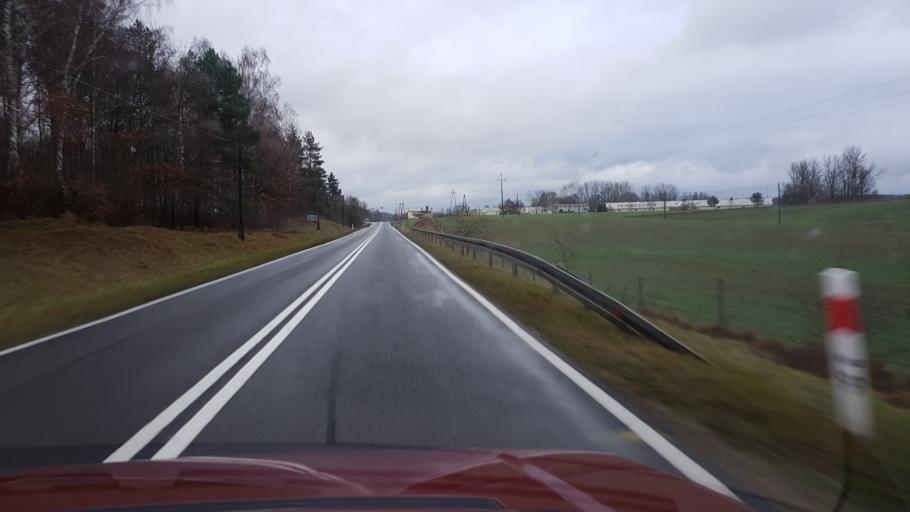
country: PL
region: West Pomeranian Voivodeship
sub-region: Powiat lobeski
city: Wegorzyno
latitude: 53.5173
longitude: 15.6370
